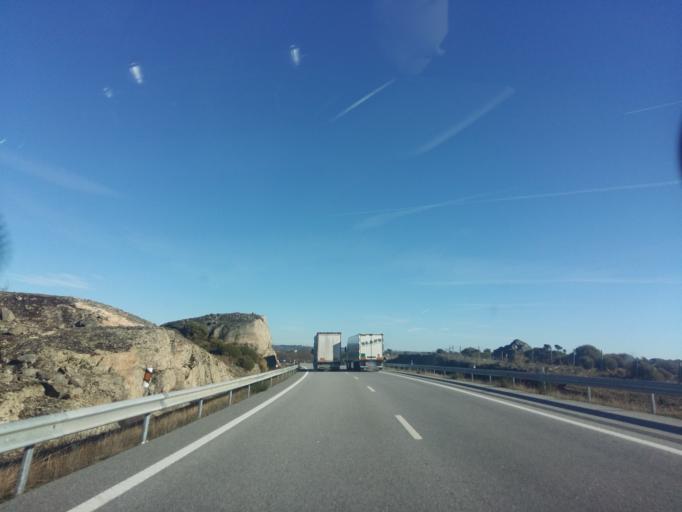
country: PT
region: Guarda
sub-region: Guarda
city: Sequeira
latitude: 40.6011
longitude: -7.0916
